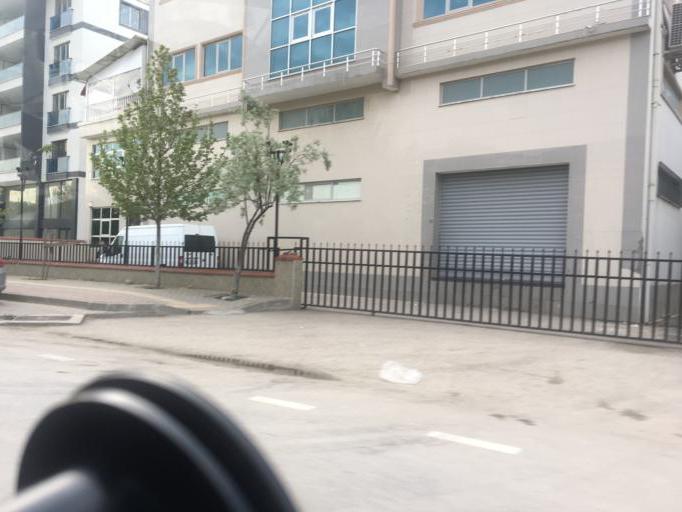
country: TR
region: Bursa
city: Yildirim
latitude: 40.2111
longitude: 29.0397
